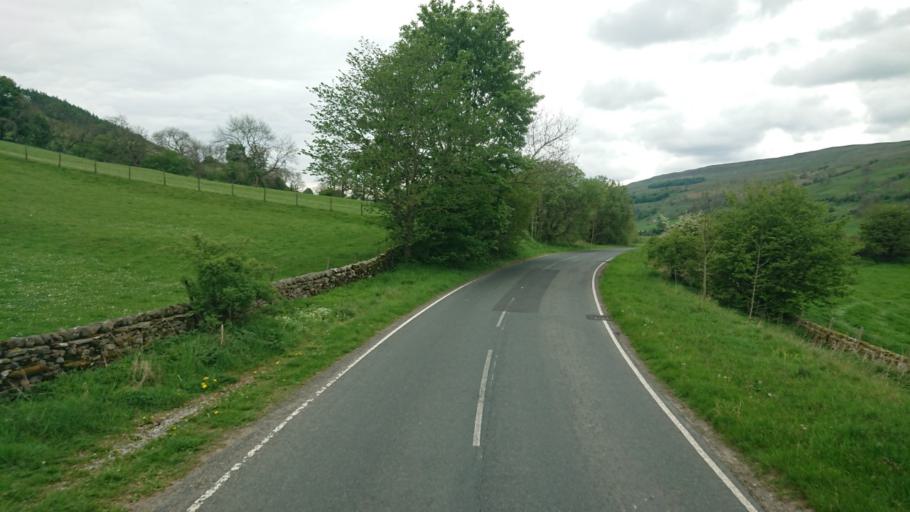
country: GB
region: England
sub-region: North Yorkshire
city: Leyburn
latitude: 54.2615
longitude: -2.0200
